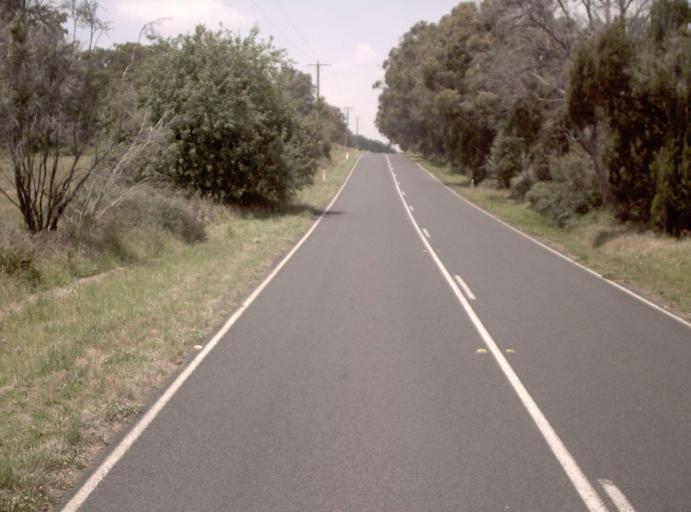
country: AU
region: Victoria
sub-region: Latrobe
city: Traralgon
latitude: -38.2553
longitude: 146.6758
